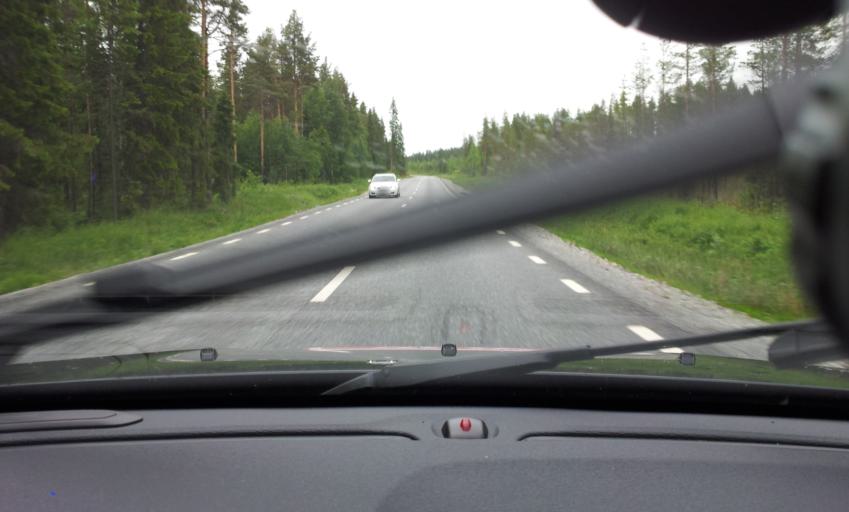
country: SE
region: Jaemtland
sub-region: OEstersunds Kommun
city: Lit
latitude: 63.7040
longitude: 14.6889
